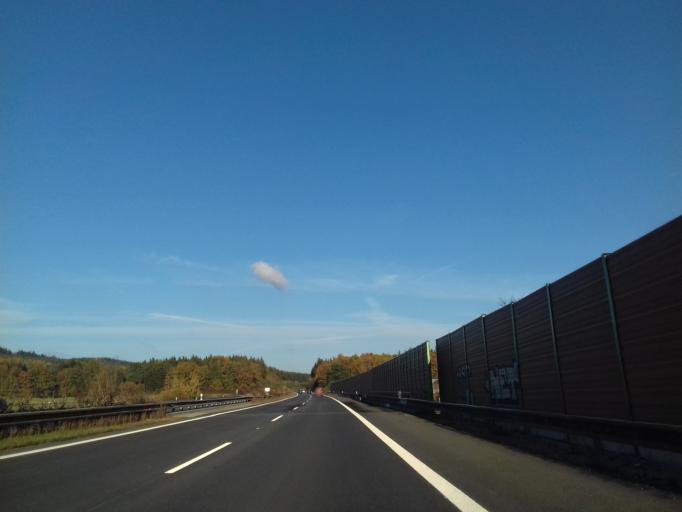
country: CZ
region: Plzensky
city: Holoubkov
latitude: 49.7640
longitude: 13.6430
